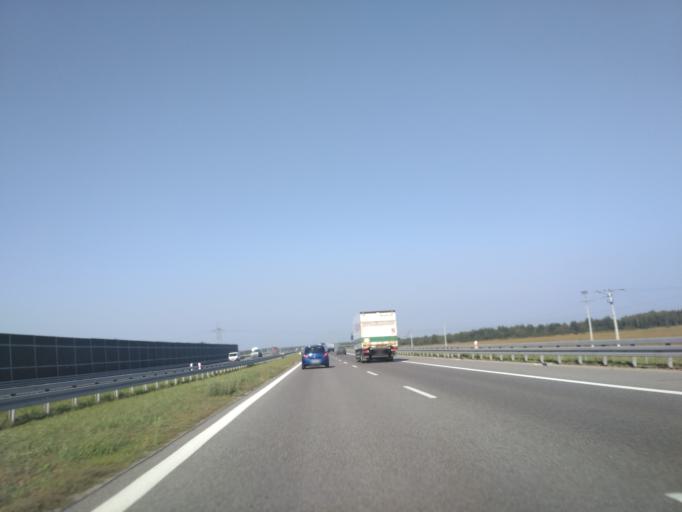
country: PL
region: Subcarpathian Voivodeship
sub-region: Powiat rzeszowski
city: Swilcza
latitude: 50.1067
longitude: 21.8888
